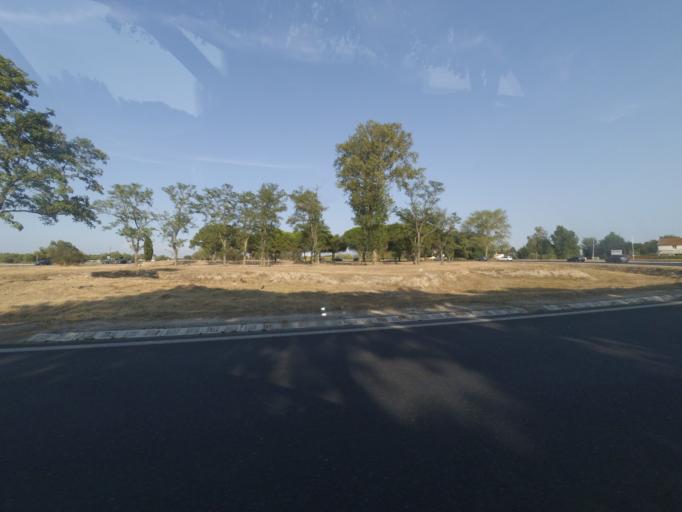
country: FR
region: Languedoc-Roussillon
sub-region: Departement du Gard
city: Le Grau-du-Roi
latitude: 43.5600
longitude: 4.1523
